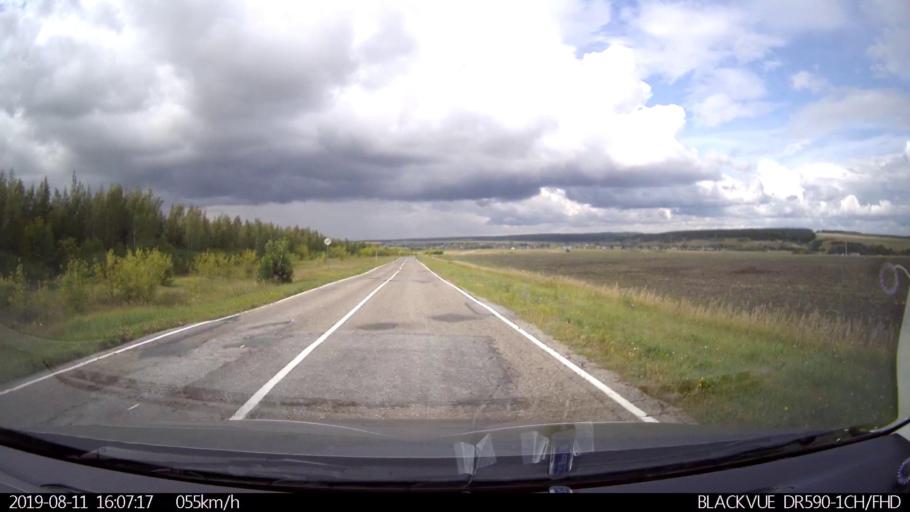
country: RU
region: Ulyanovsk
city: Ignatovka
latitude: 53.9750
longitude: 47.6491
